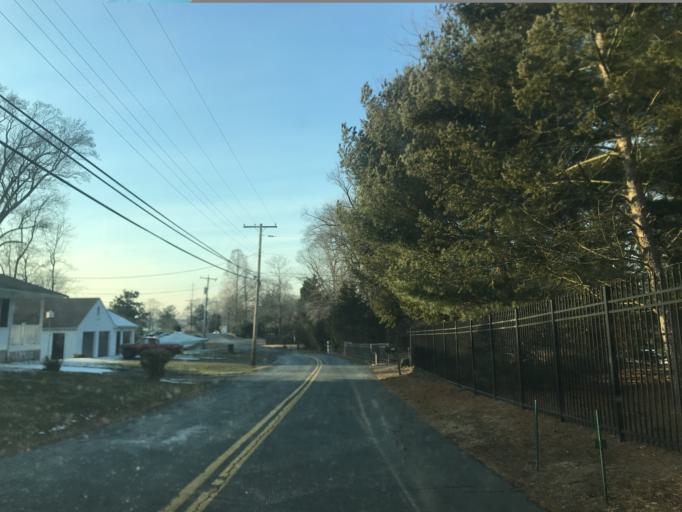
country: US
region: Maryland
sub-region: Harford County
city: Riverside
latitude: 39.4407
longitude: -76.2541
